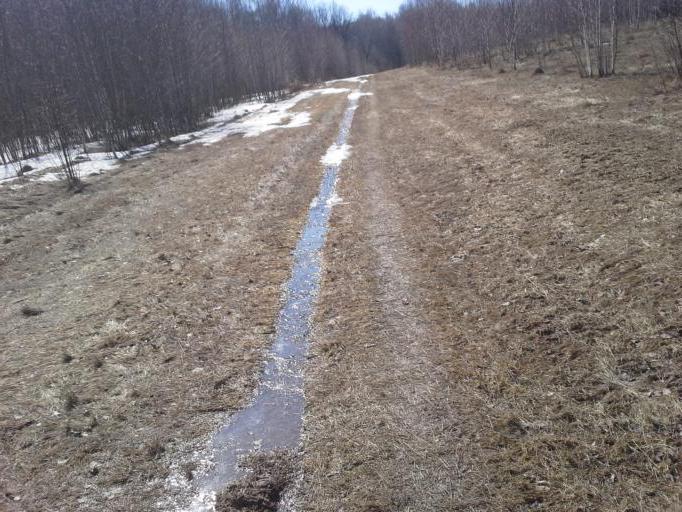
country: RU
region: Moscow
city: Yasenevo
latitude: 55.5814
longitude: 37.5420
